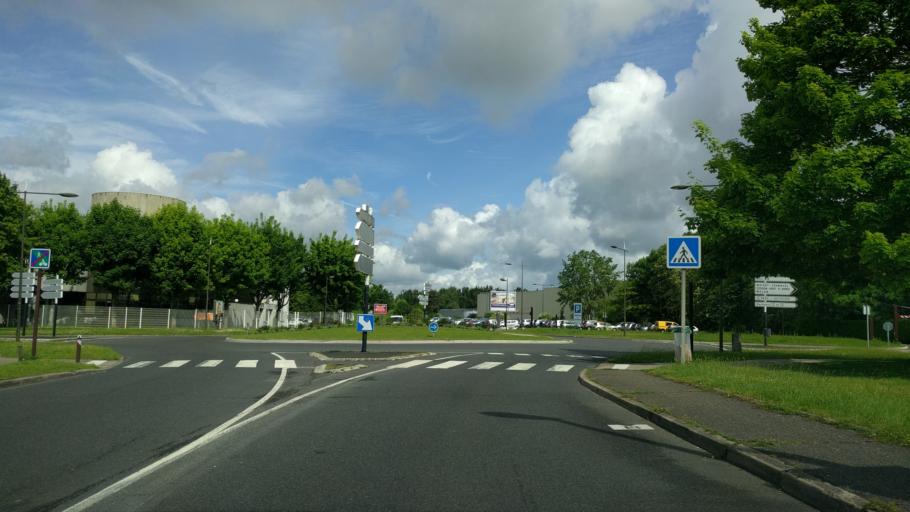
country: FR
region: Ile-de-France
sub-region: Departement de Seine-et-Marne
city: Savigny-le-Temple
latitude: 48.5962
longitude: 2.5883
